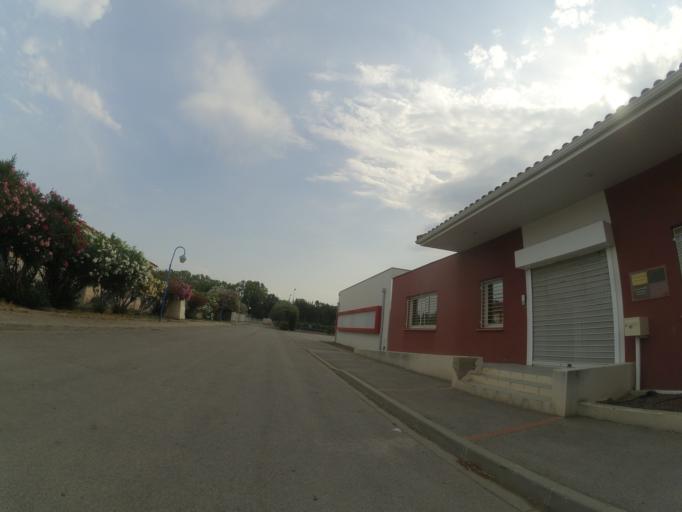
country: FR
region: Languedoc-Roussillon
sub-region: Departement des Pyrenees-Orientales
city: Corneilla-la-Riviere
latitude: 42.6826
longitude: 2.7346
